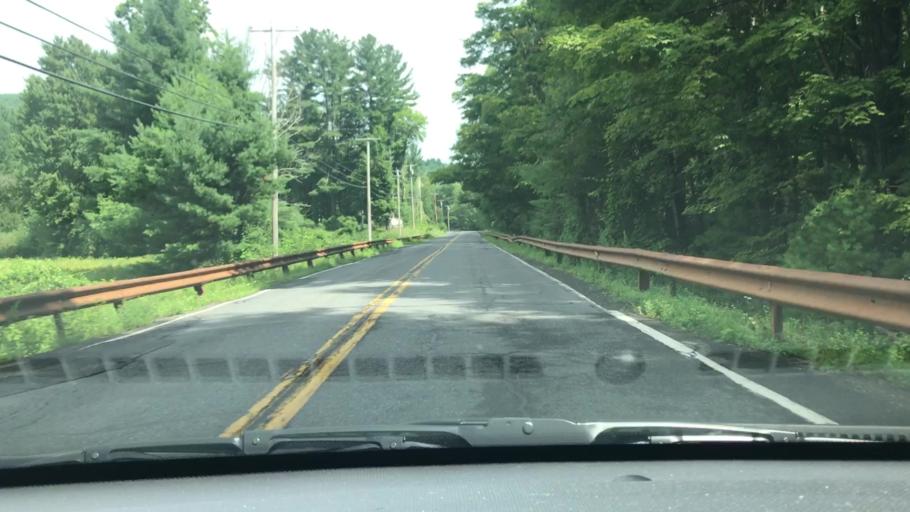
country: US
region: New York
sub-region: Ulster County
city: Shokan
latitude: 41.9724
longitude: -74.2772
